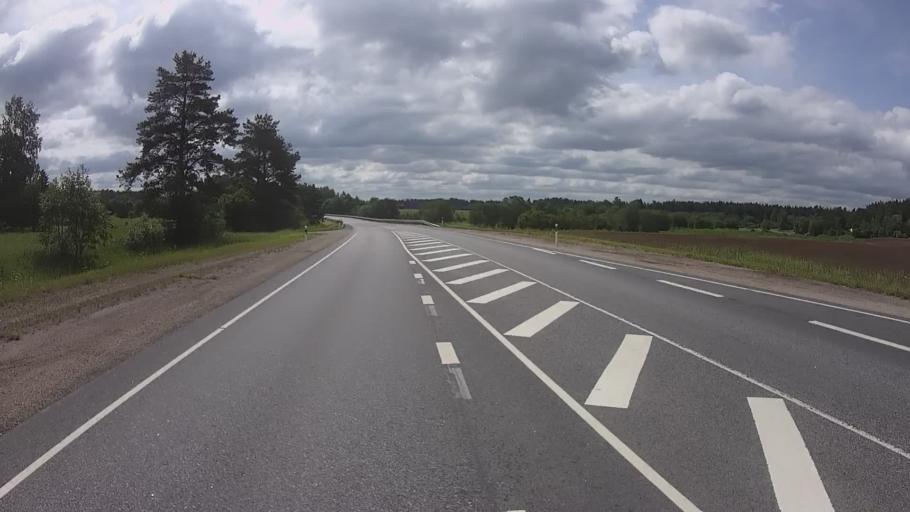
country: EE
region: Polvamaa
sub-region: Polva linn
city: Polva
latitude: 58.1490
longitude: 26.9400
